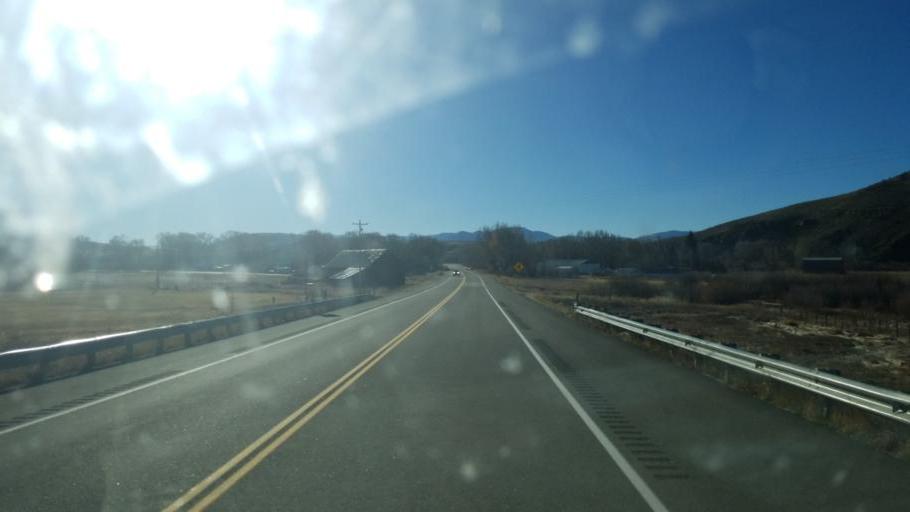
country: US
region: Colorado
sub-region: Gunnison County
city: Gunnison
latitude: 38.5048
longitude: -106.7304
